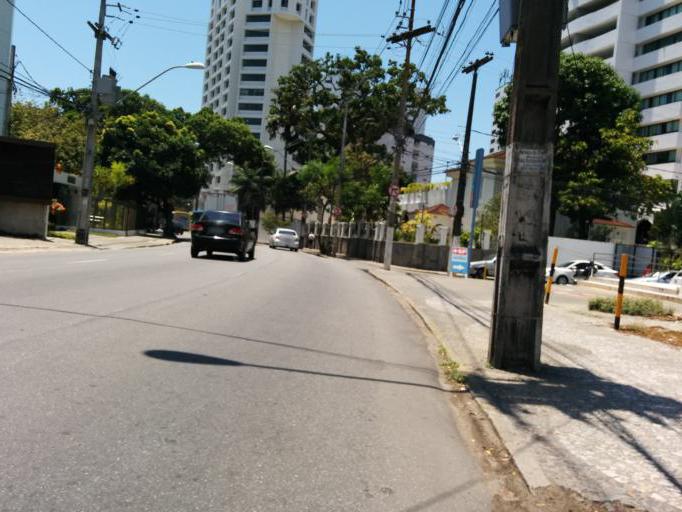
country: BR
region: Pernambuco
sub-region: Recife
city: Recife
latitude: -8.0459
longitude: -34.9020
